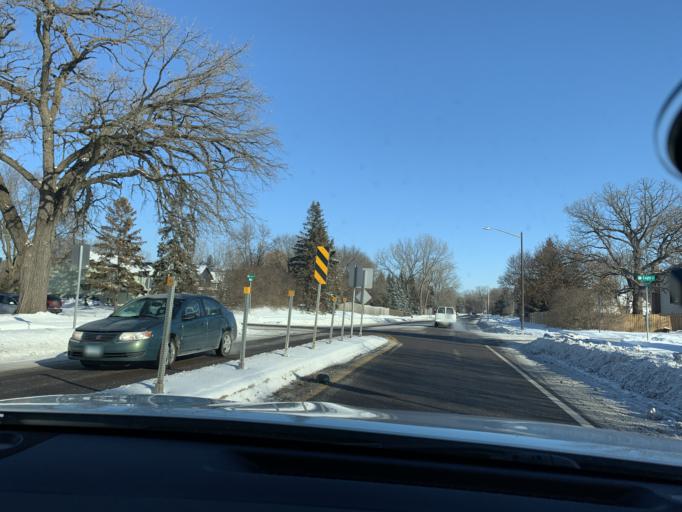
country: US
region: Minnesota
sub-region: Anoka County
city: Coon Rapids
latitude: 45.1574
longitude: -93.3033
